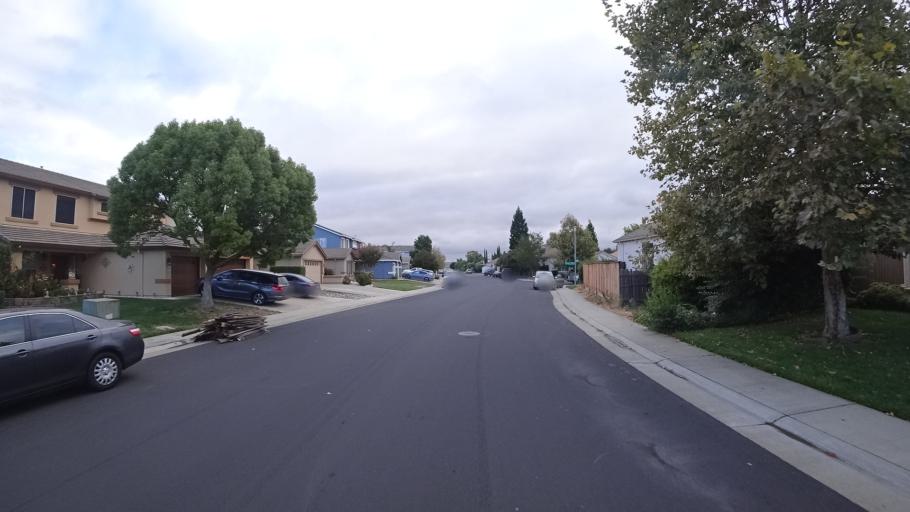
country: US
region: California
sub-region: Sacramento County
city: Laguna
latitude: 38.4348
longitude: -121.4253
